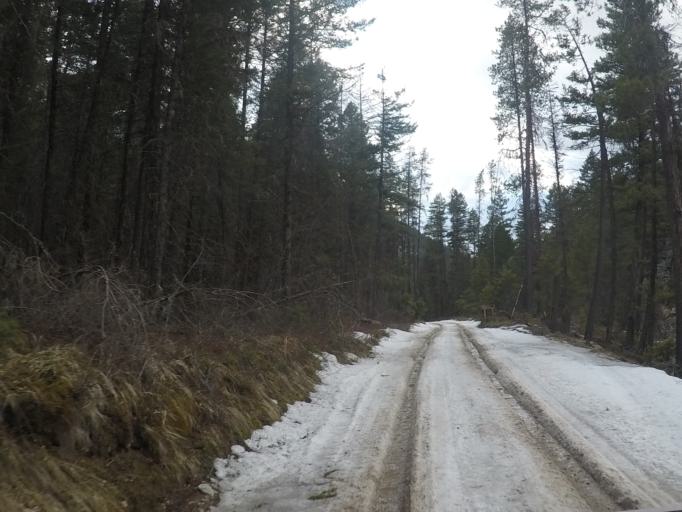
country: US
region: Montana
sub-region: Missoula County
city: Clinton
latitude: 46.5606
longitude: -113.7022
